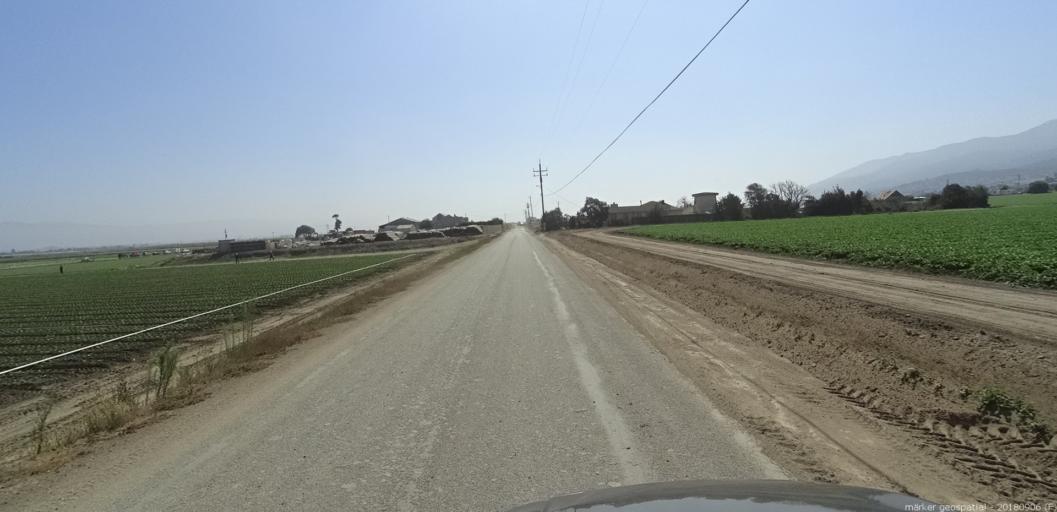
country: US
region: California
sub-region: Monterey County
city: Chualar
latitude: 36.5969
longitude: -121.6044
